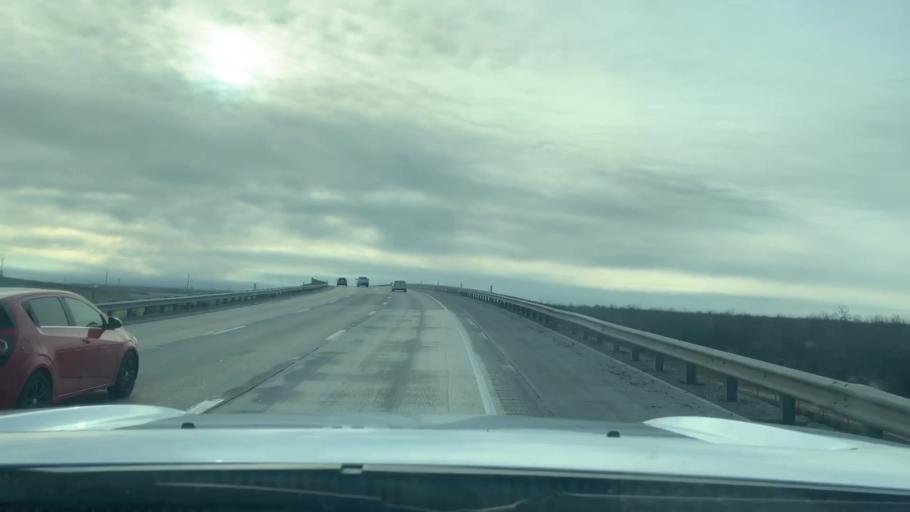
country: US
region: California
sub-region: Kern County
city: McFarland
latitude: 35.5937
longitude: -119.2090
